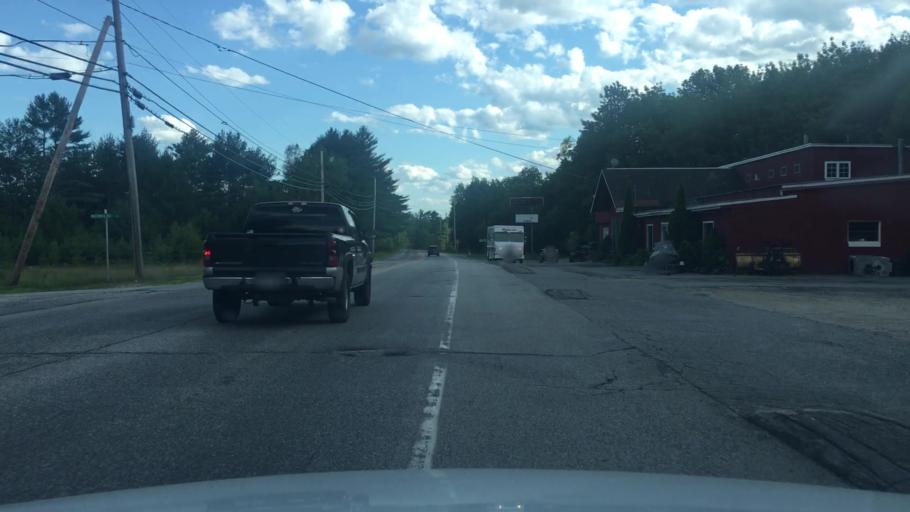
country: US
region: Maine
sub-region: Franklin County
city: Wilton
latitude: 44.5681
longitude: -70.2310
